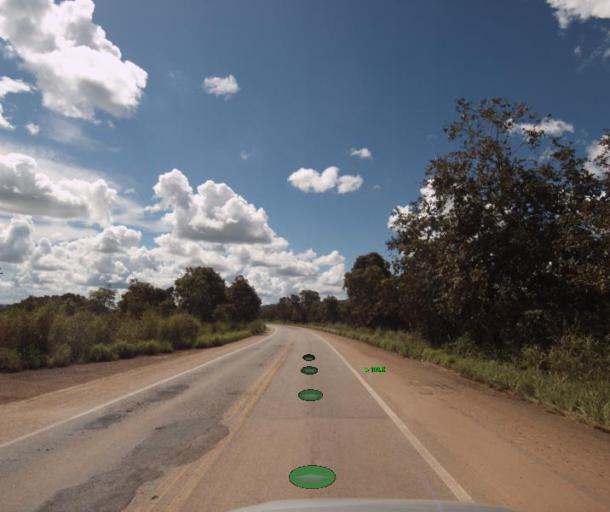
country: BR
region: Goias
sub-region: Porangatu
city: Porangatu
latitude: -13.6812
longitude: -49.0235
